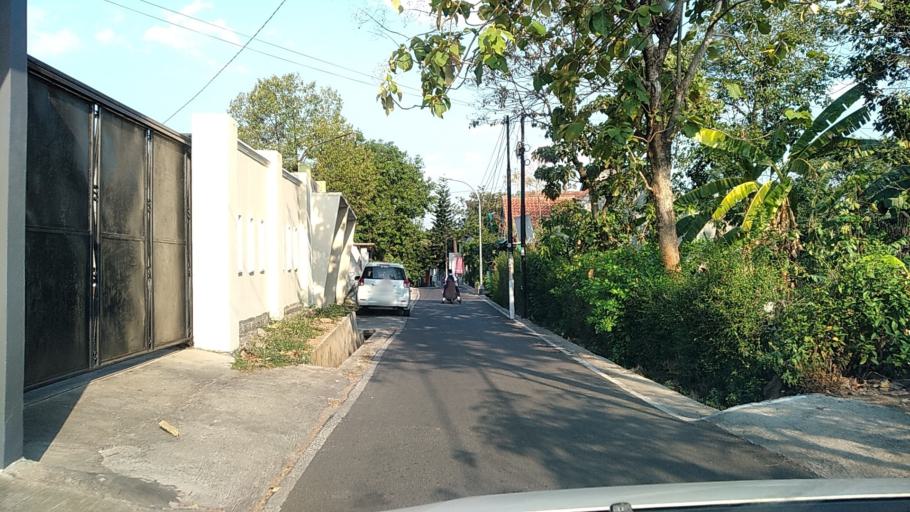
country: ID
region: Central Java
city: Ungaran
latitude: -7.0699
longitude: 110.4303
